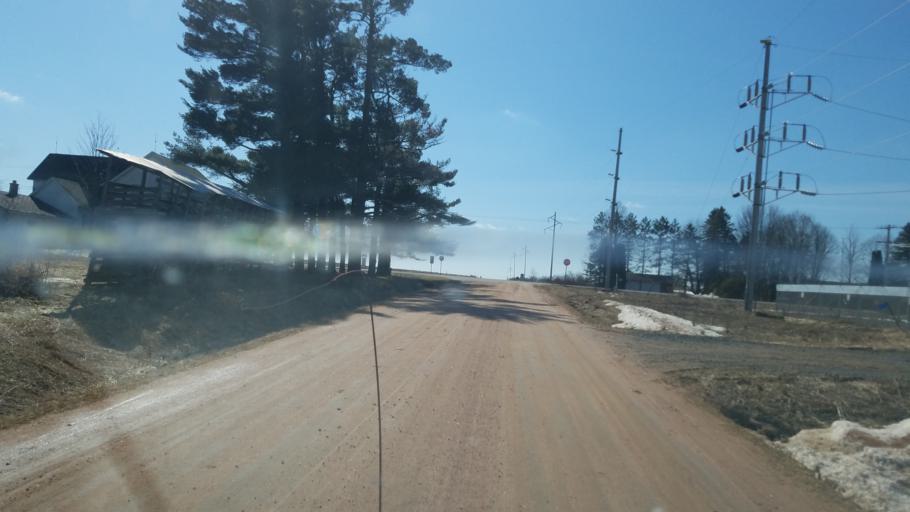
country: US
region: Wisconsin
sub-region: Clark County
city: Loyal
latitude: 44.5834
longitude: -90.3957
